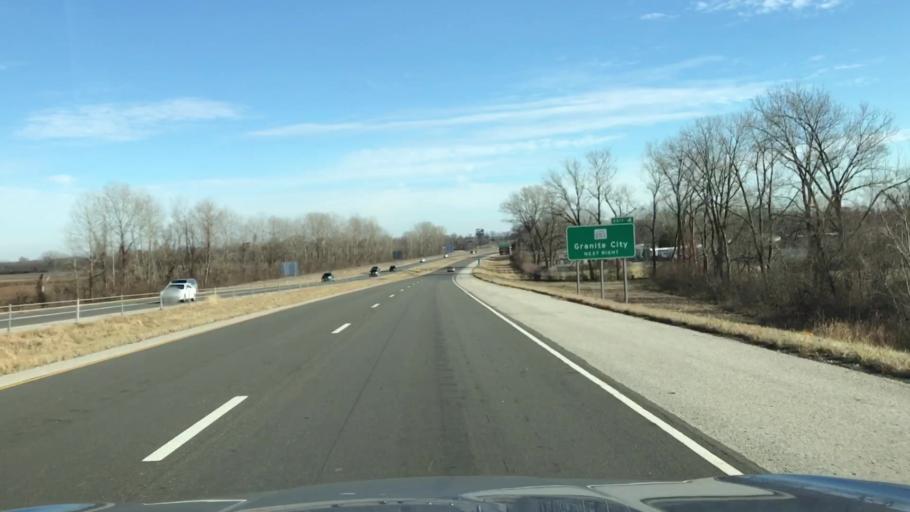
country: US
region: Illinois
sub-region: Madison County
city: Mitchell
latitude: 38.7652
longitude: -90.1117
